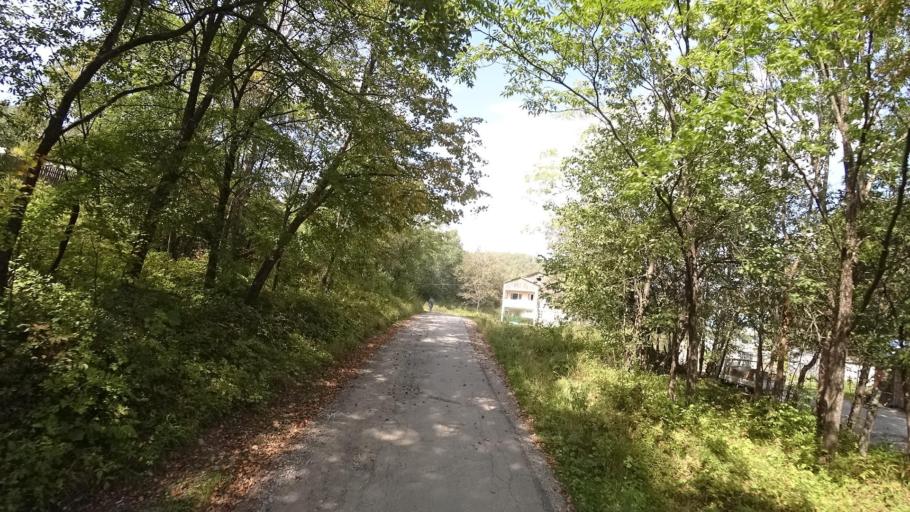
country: RU
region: Jewish Autonomous Oblast
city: Londoko
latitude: 49.0257
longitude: 131.9223
